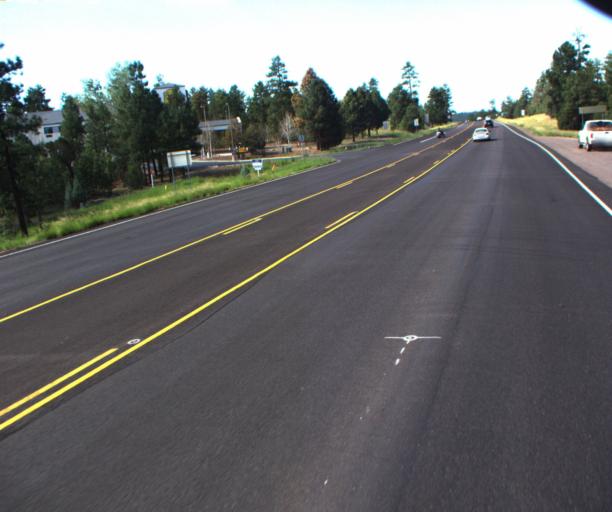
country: US
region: Arizona
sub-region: Navajo County
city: Show Low
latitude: 34.2399
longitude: -110.0602
